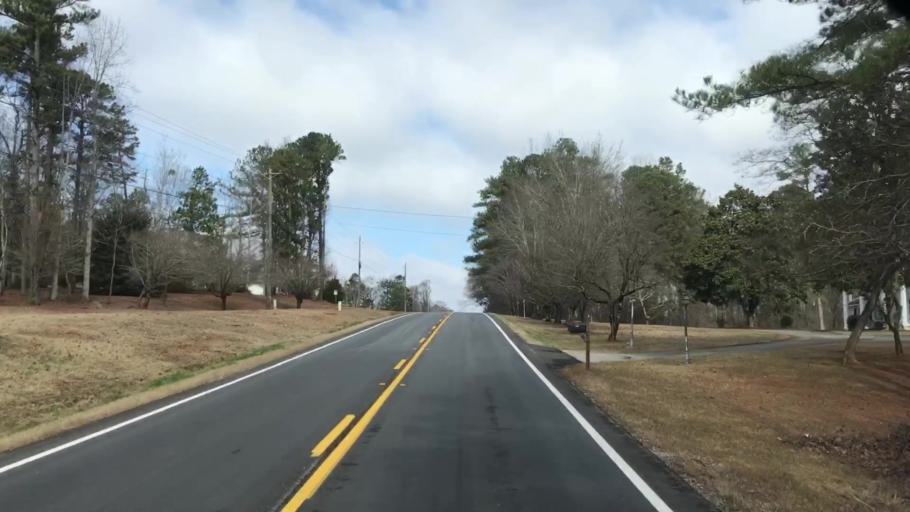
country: US
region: Georgia
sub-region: Jackson County
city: Braselton
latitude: 34.1510
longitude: -83.8371
